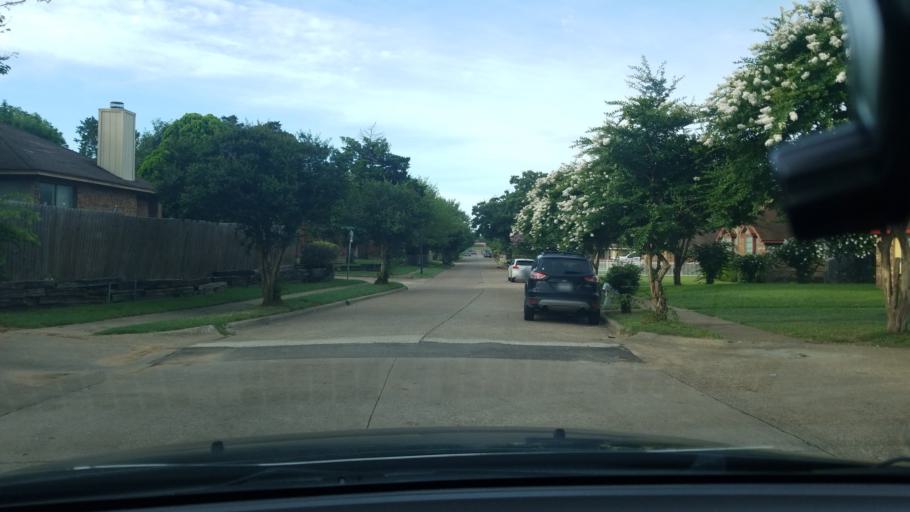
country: US
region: Texas
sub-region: Dallas County
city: Balch Springs
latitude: 32.7568
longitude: -96.6475
